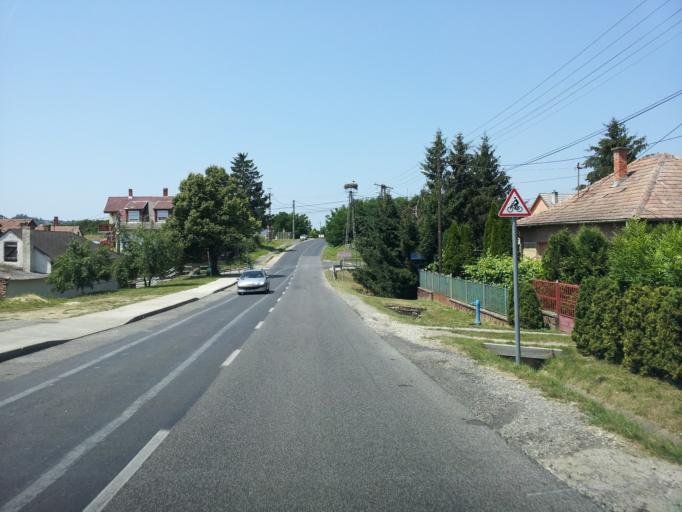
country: HU
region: Zala
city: Zalaegerszeg
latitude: 46.8570
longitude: 16.8279
